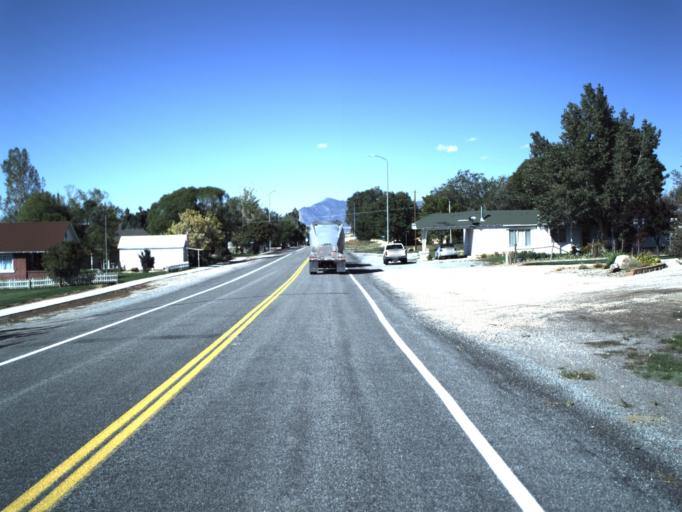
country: US
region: Utah
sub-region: Millard County
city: Fillmore
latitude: 39.1011
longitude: -112.2709
